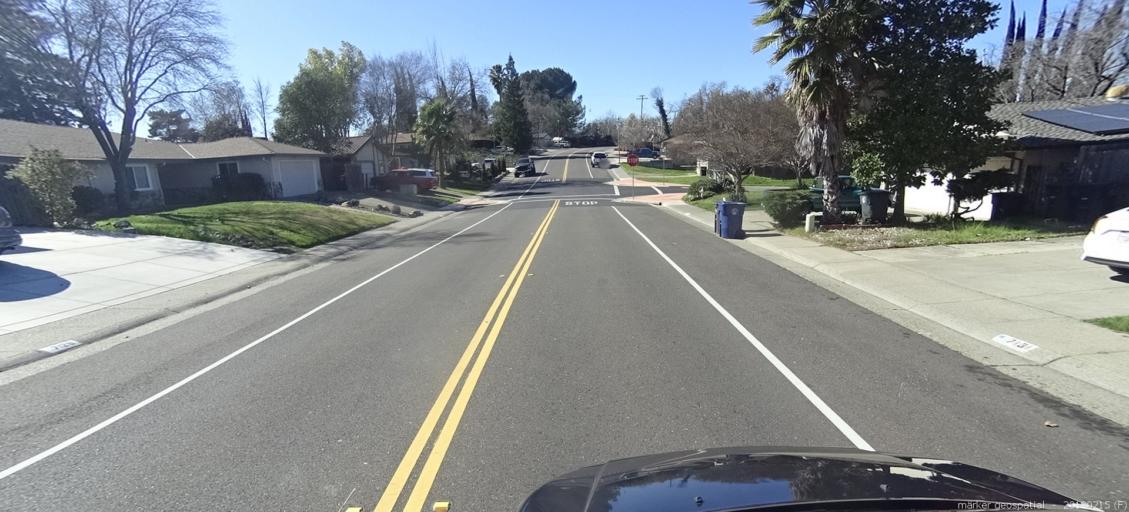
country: US
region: California
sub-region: Sacramento County
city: Fair Oaks
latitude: 38.6708
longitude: -121.2977
